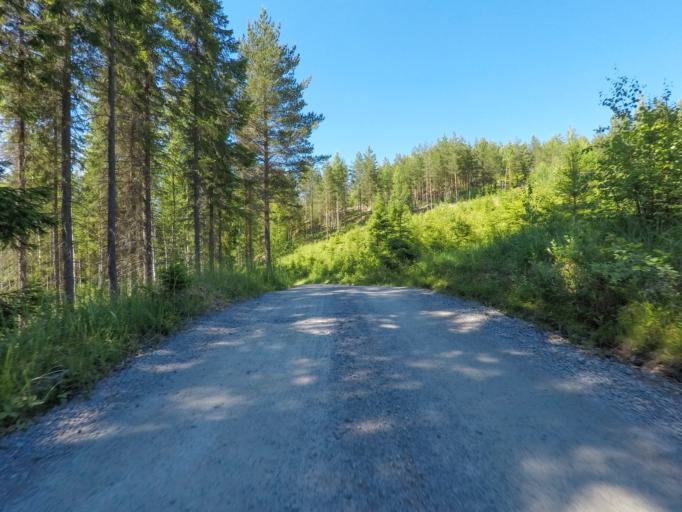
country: FI
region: Southern Savonia
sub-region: Savonlinna
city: Rantasalmi
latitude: 62.1732
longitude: 28.2444
